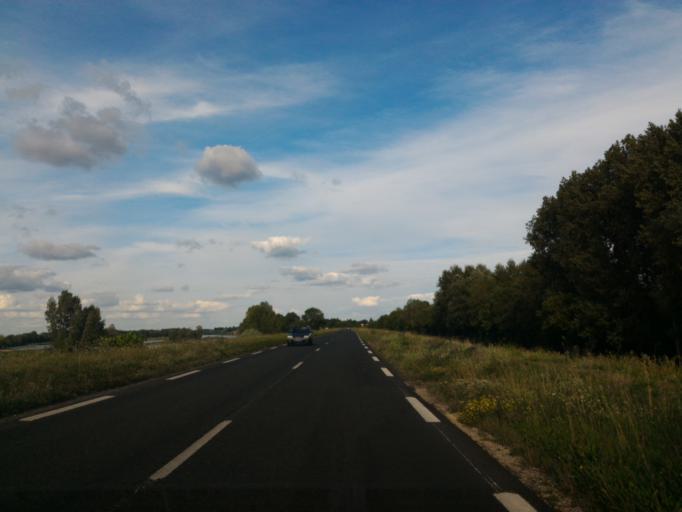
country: FR
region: Centre
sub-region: Departement du Loir-et-Cher
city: Suevres
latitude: 47.6522
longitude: 1.4658
